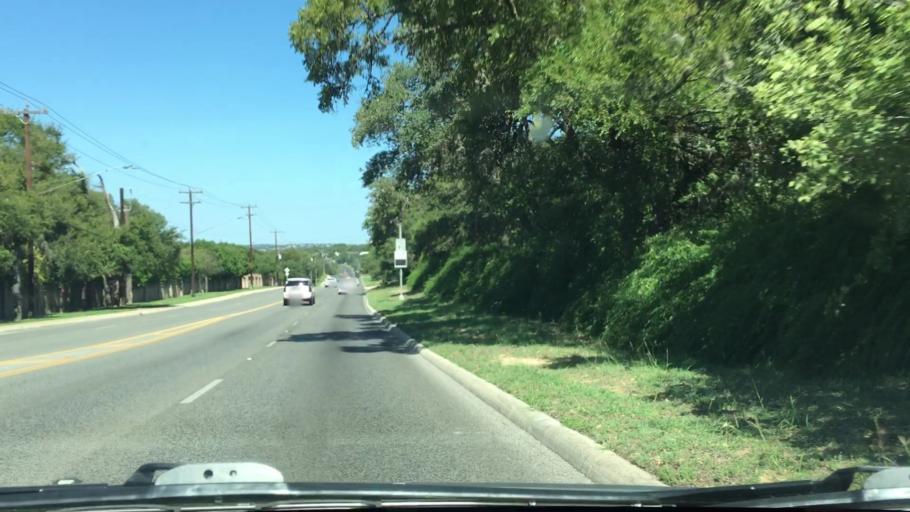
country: US
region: Texas
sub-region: Bexar County
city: Hollywood Park
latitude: 29.5750
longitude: -98.4953
